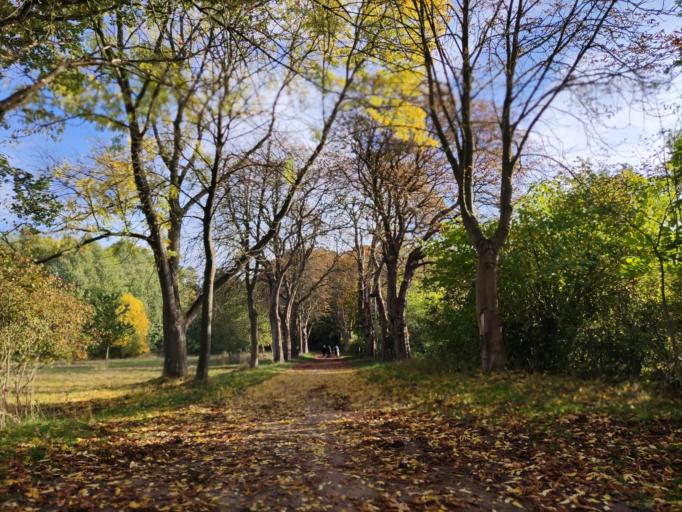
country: DE
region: Lower Saxony
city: Lueneburg
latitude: 53.2421
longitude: 10.4308
